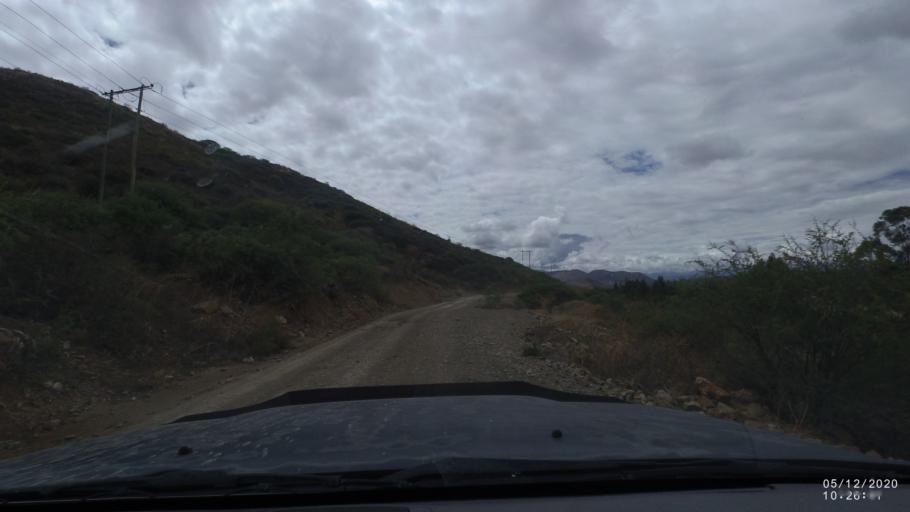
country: BO
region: Cochabamba
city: Sipe Sipe
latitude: -17.5277
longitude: -66.2816
